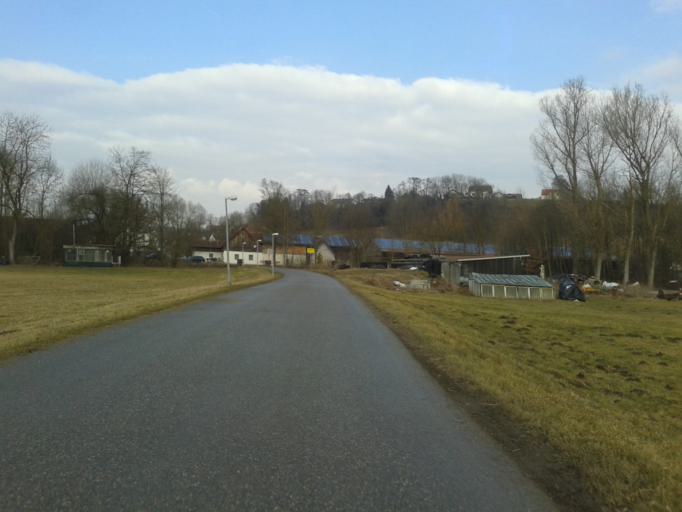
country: DE
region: Baden-Wuerttemberg
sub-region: Tuebingen Region
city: Ersingen
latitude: 48.3120
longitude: 9.8670
